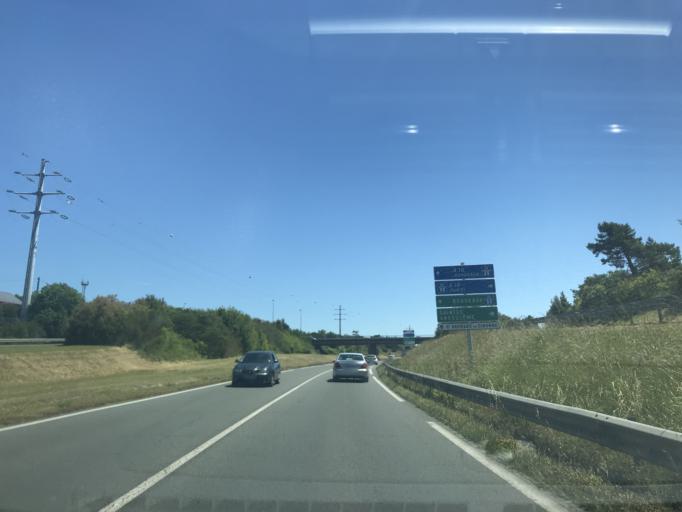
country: FR
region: Poitou-Charentes
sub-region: Departement de la Charente-Maritime
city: Saint-Georges-de-Didonne
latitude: 45.6275
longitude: -1.0008
